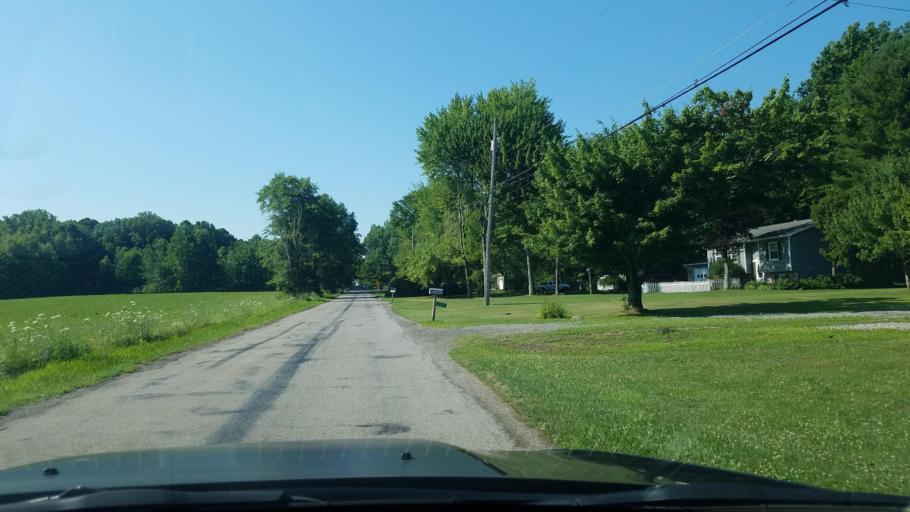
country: US
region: Ohio
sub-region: Trumbull County
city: Leavittsburg
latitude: 41.2968
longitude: -80.9059
